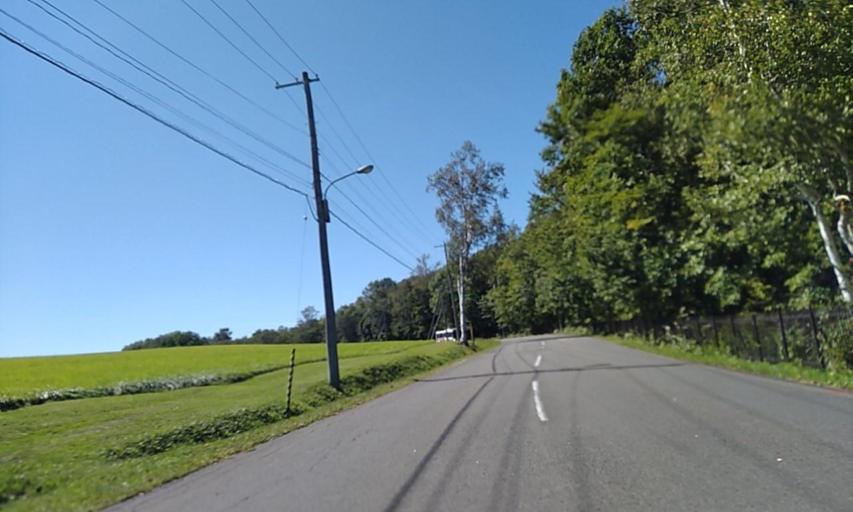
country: JP
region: Hokkaido
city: Sapporo
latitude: 43.0022
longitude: 141.3936
